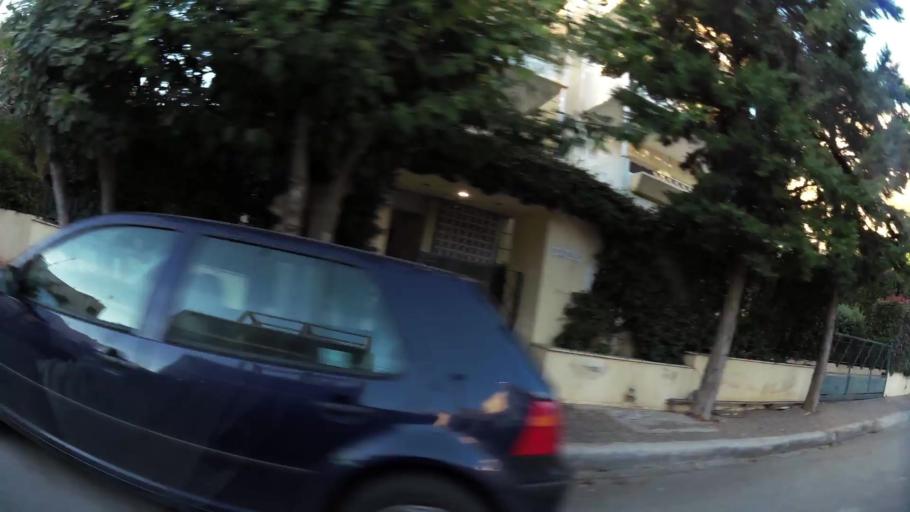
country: GR
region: Attica
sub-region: Nomarchia Athinas
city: Kifisia
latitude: 38.0836
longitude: 23.8205
